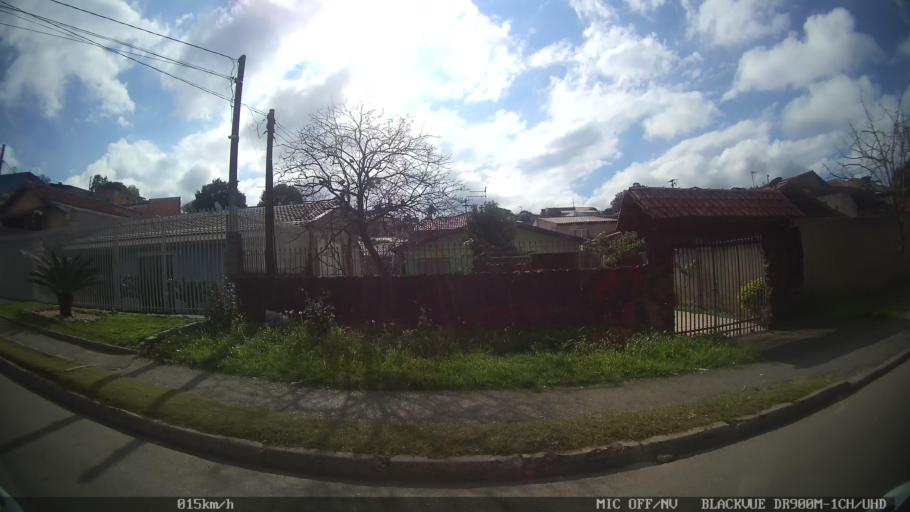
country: BR
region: Parana
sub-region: Colombo
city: Colombo
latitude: -25.3577
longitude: -49.1872
